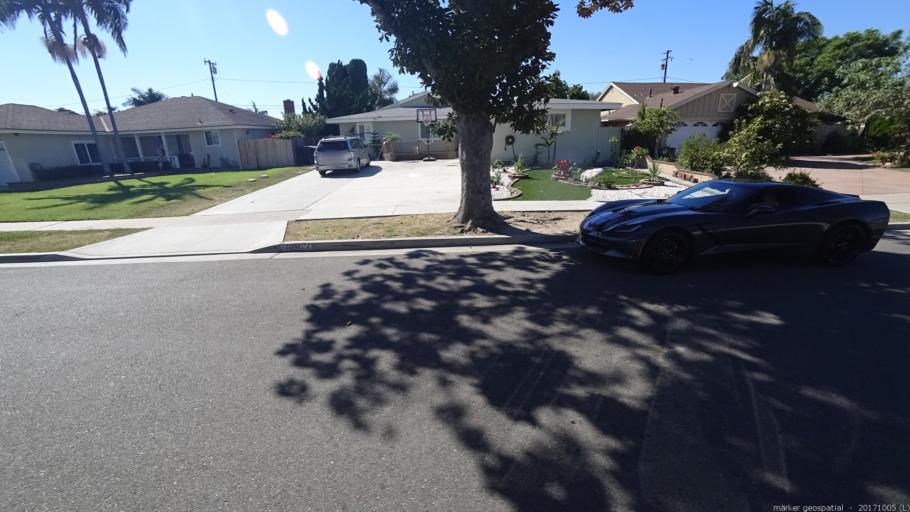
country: US
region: California
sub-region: Orange County
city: Garden Grove
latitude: 33.7878
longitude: -117.9434
